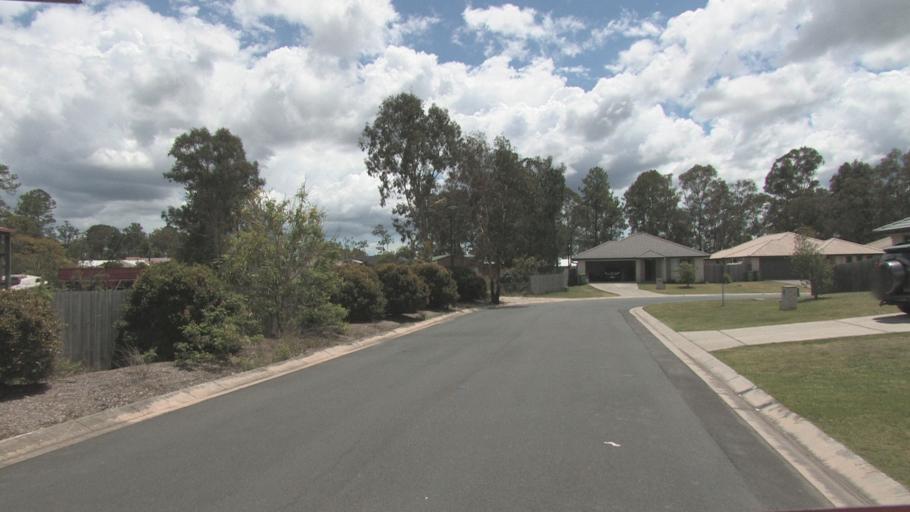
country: AU
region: Queensland
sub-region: Logan
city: Waterford West
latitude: -27.6830
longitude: 153.1282
